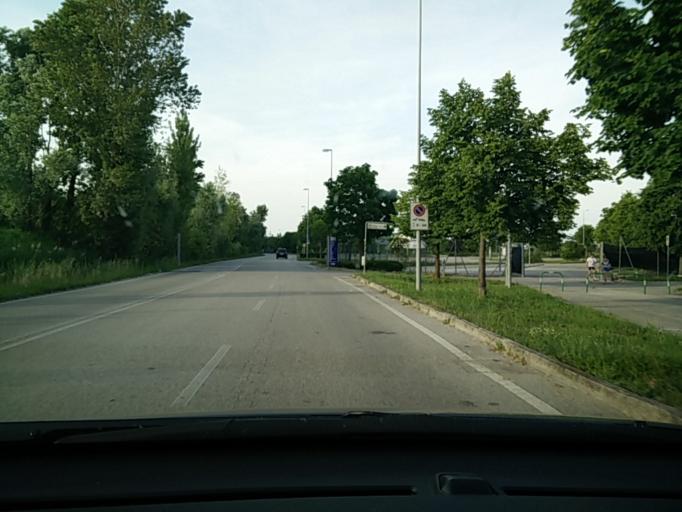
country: IT
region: Veneto
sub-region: Provincia di Padova
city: Limena
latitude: 45.4338
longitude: 11.8563
